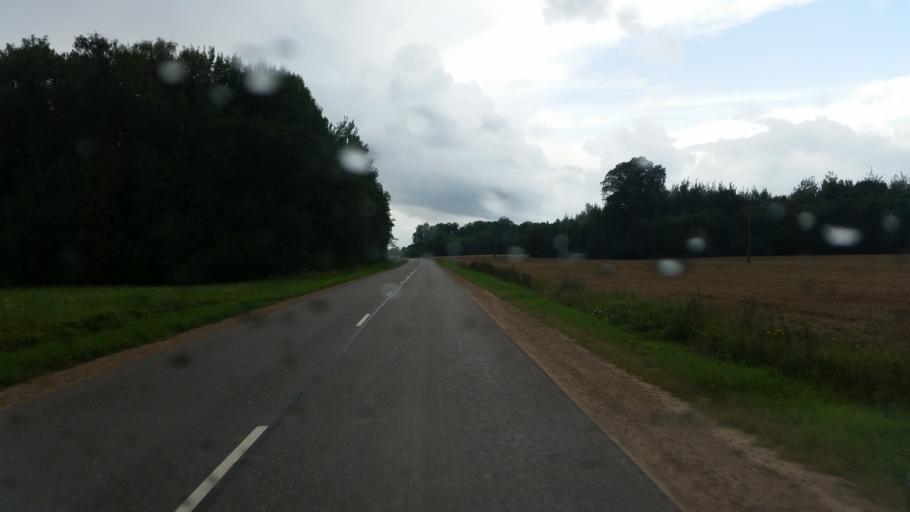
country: LV
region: Vecumnieki
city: Vecumnieki
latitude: 56.4321
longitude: 24.4456
